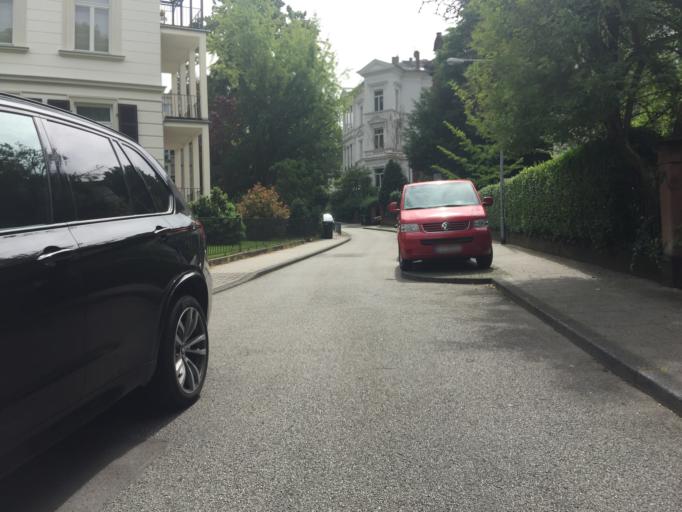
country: DE
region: Hesse
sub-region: Regierungsbezirk Darmstadt
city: Wiesbaden
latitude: 50.0797
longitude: 8.2488
